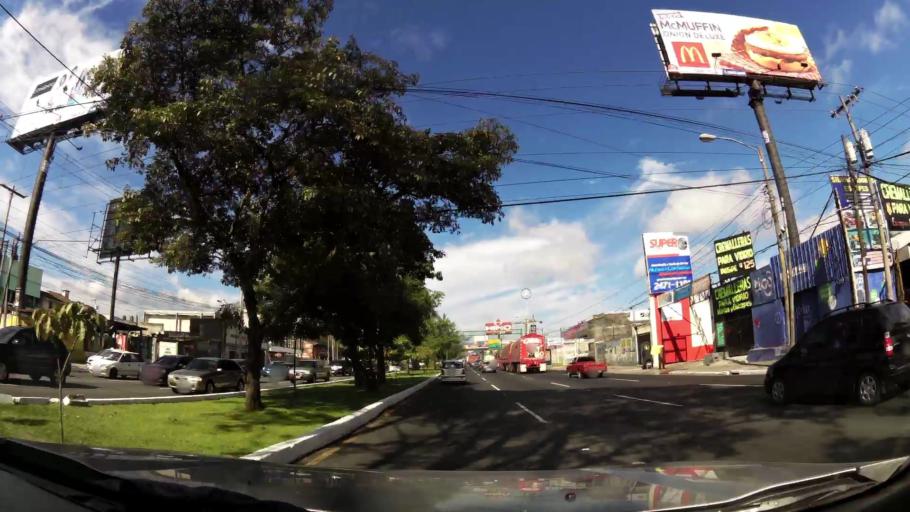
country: GT
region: Guatemala
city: Guatemala City
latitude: 14.6204
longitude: -90.5469
